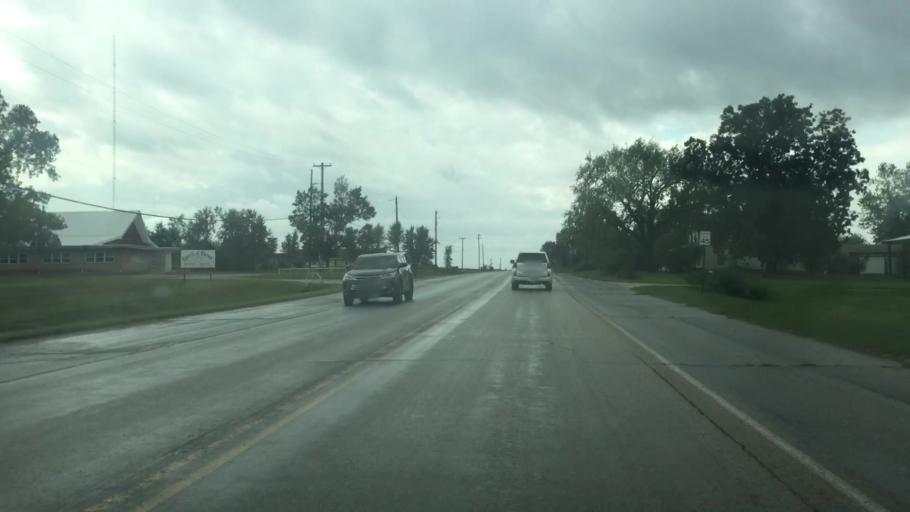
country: US
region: Kansas
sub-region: Allen County
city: Iola
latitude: 37.8995
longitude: -95.4094
